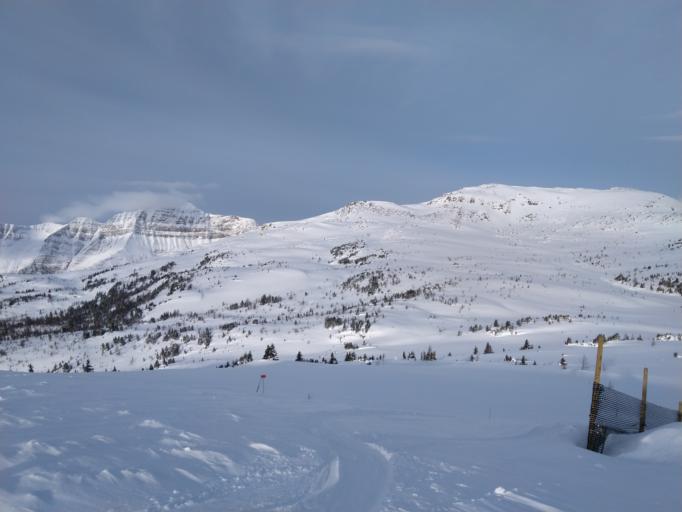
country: CA
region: Alberta
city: Banff
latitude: 51.0710
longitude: -115.7869
